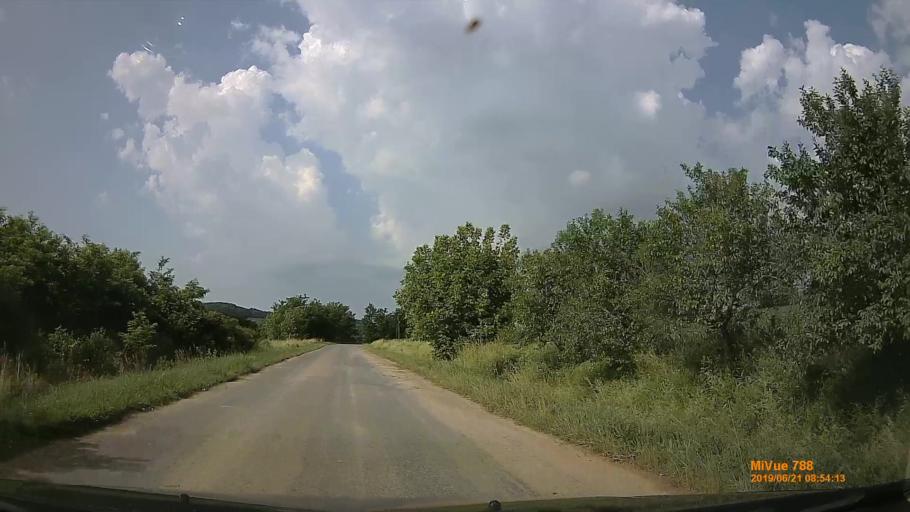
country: HU
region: Baranya
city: Buekkoesd
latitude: 46.1658
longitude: 17.8871
